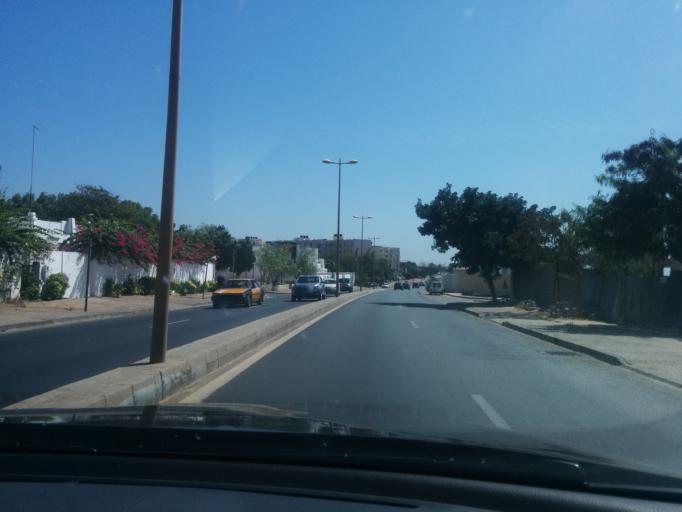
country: SN
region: Dakar
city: Mermoz Boabab
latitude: 14.7079
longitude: -17.4853
